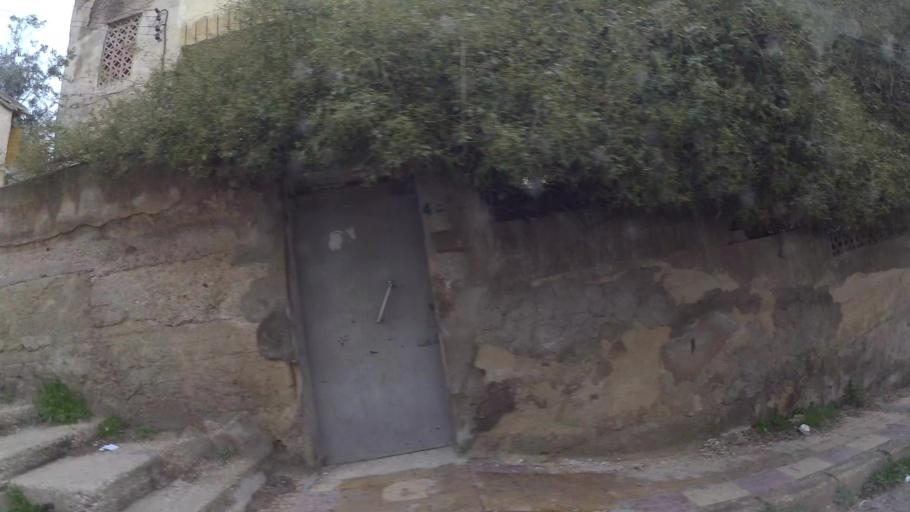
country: JO
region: Amman
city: Amman
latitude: 31.9672
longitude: 35.9319
